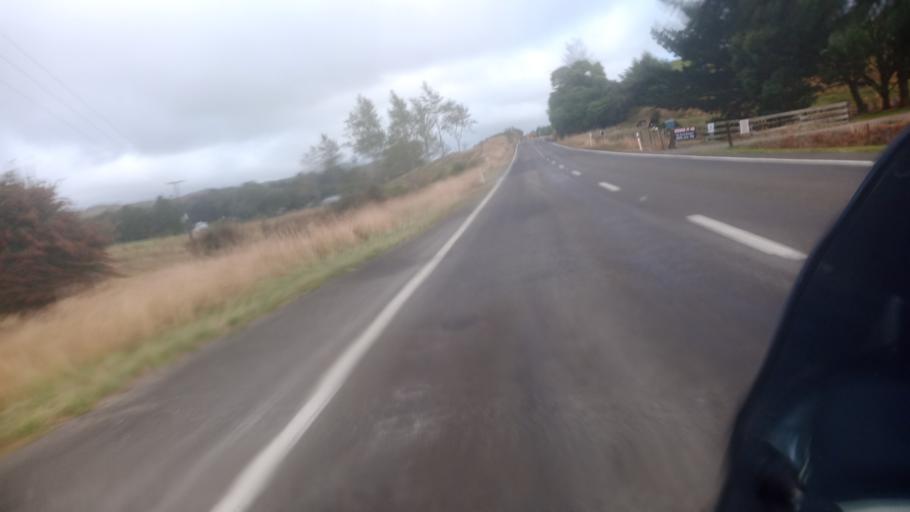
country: NZ
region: Bay of Plenty
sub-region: Opotiki District
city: Opotiki
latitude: -38.3810
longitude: 177.5526
